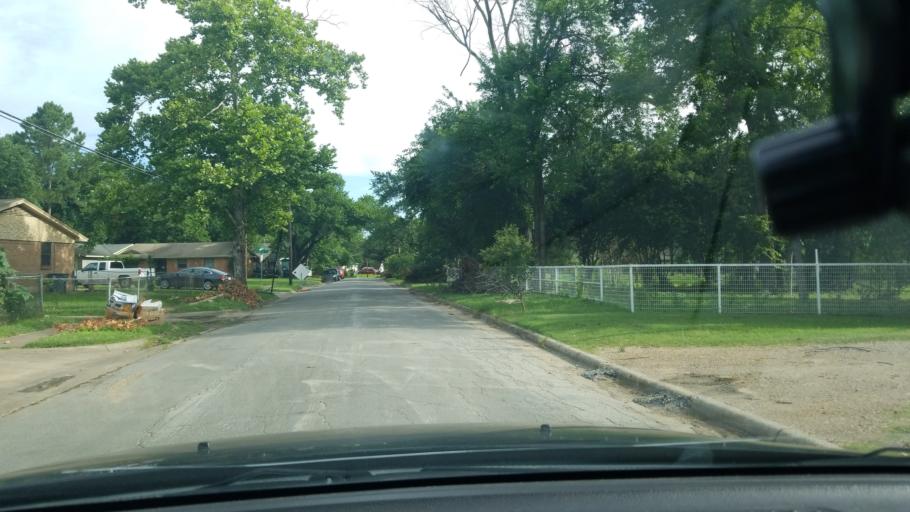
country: US
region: Texas
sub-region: Dallas County
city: Balch Springs
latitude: 32.7582
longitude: -96.6694
